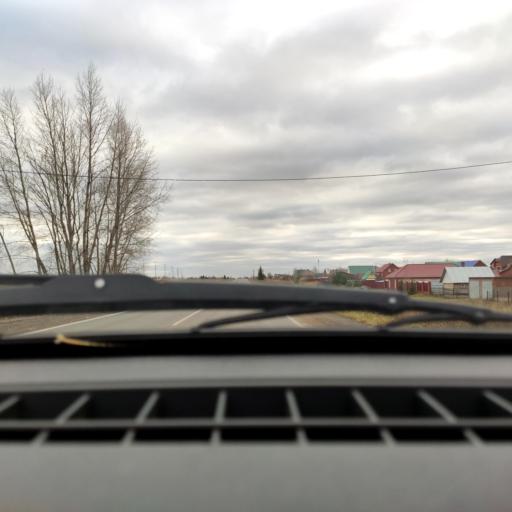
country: RU
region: Bashkortostan
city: Iglino
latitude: 54.7847
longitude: 56.2526
